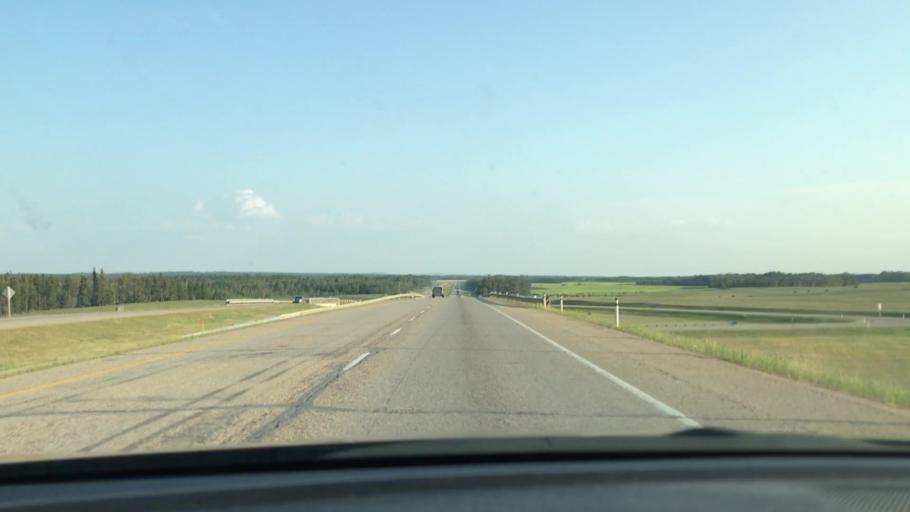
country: CA
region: Alberta
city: Ponoka
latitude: 52.5811
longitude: -113.6633
